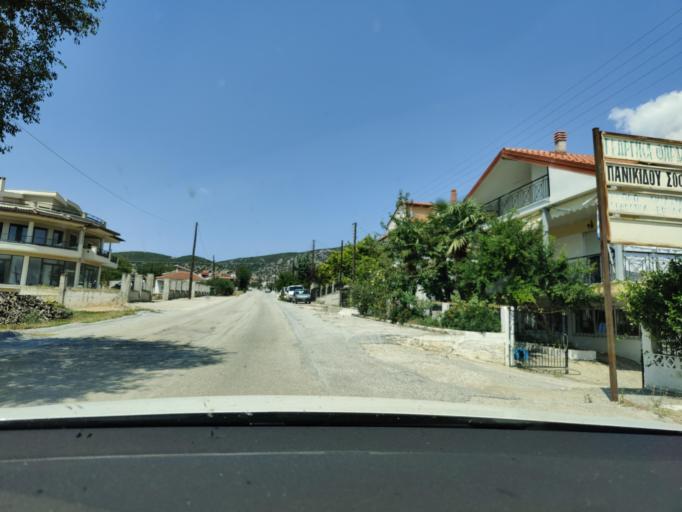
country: GR
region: East Macedonia and Thrace
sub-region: Nomos Kavalas
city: Paralia Ofryniou
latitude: 40.7981
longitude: 23.9536
